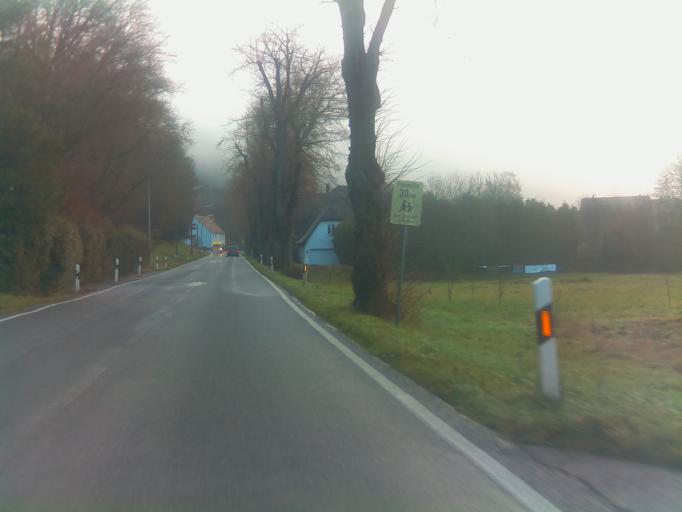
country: DE
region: Bavaria
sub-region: Regierungsbezirk Unterfranken
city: Neunkirchen
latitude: 49.6724
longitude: 9.3916
